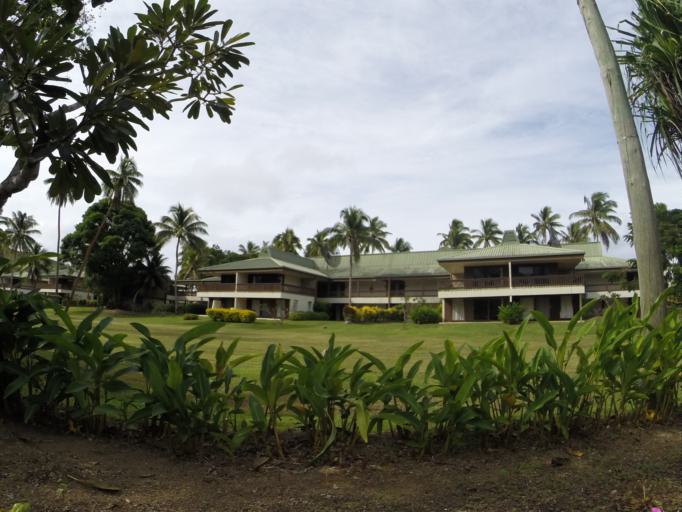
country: FJ
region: Western
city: Nadi
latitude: -18.2021
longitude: 177.6956
